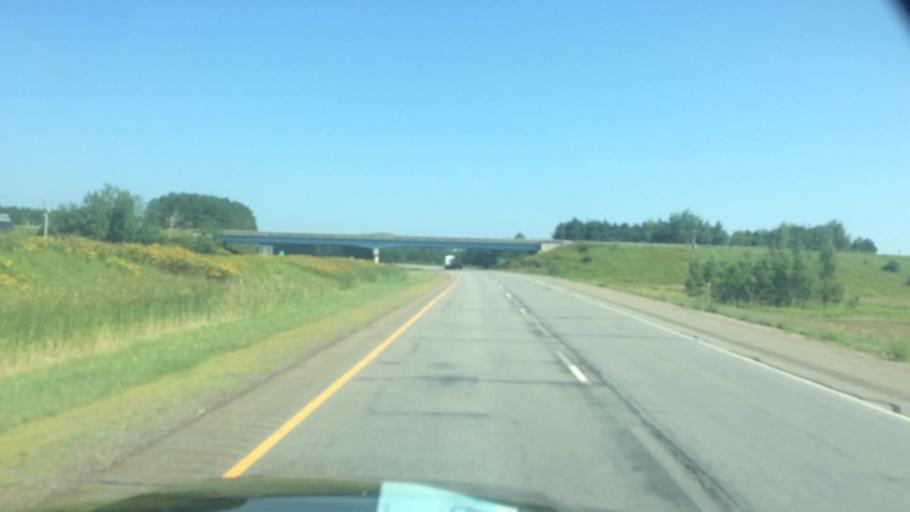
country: US
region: Wisconsin
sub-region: Lincoln County
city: Merrill
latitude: 45.1905
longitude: -89.6461
